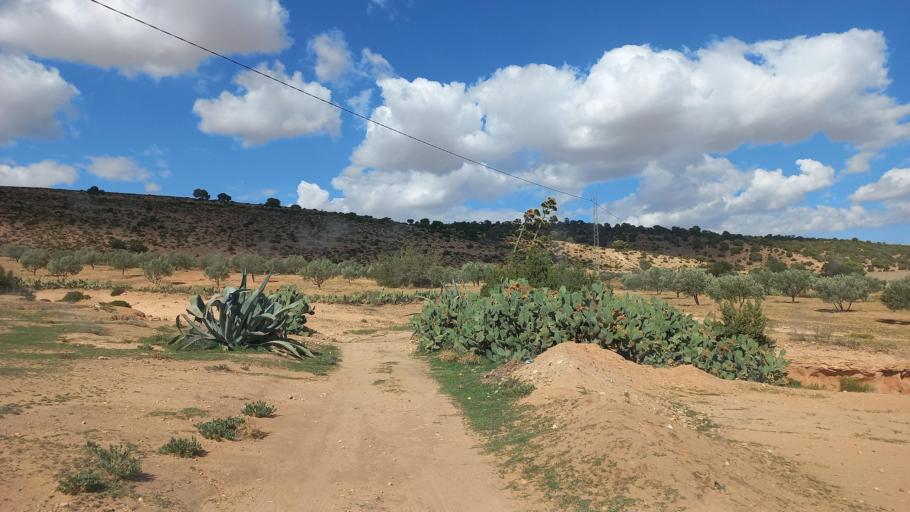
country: TN
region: Al Qasrayn
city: Kasserine
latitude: 35.3725
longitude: 8.8835
